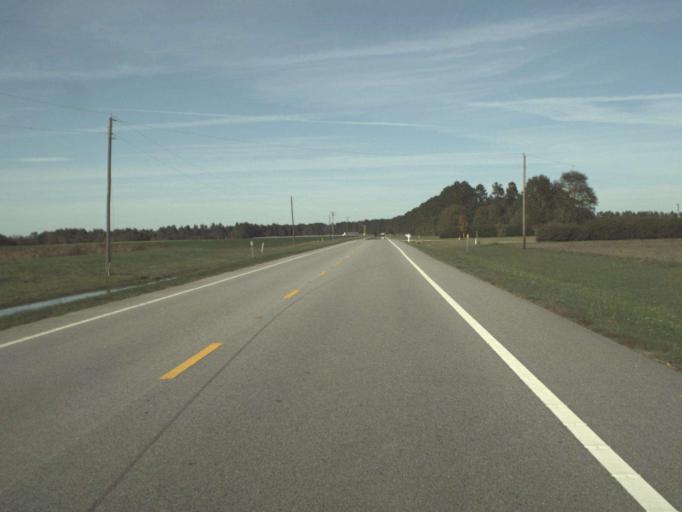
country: US
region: Florida
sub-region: Escambia County
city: Molino
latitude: 30.8322
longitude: -87.4354
